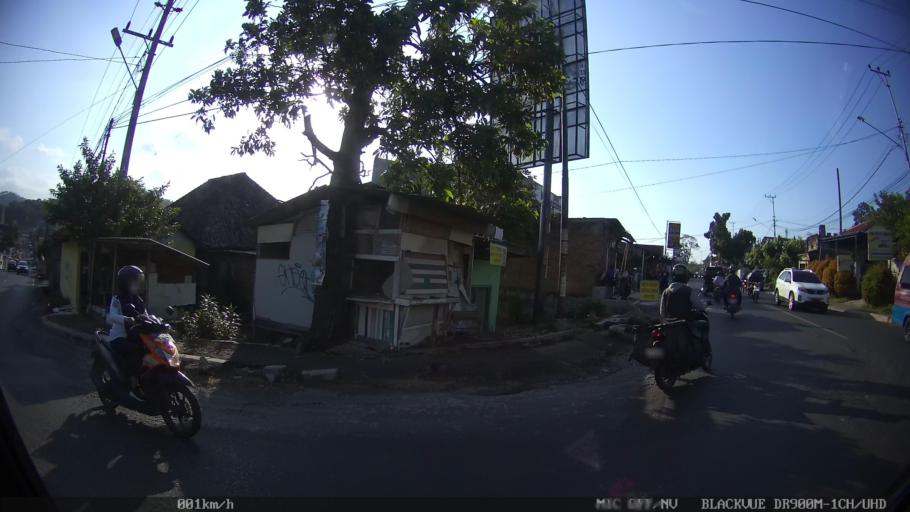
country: ID
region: Lampung
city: Bandarlampung
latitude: -5.4045
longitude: 105.2514
